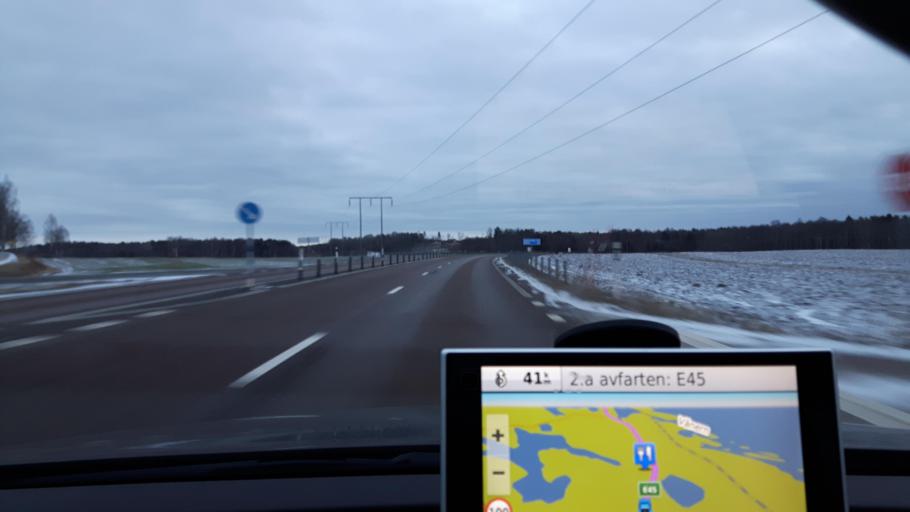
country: SE
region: Vaestra Goetaland
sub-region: Melleruds Kommun
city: Mellerud
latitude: 58.7341
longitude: 12.4599
